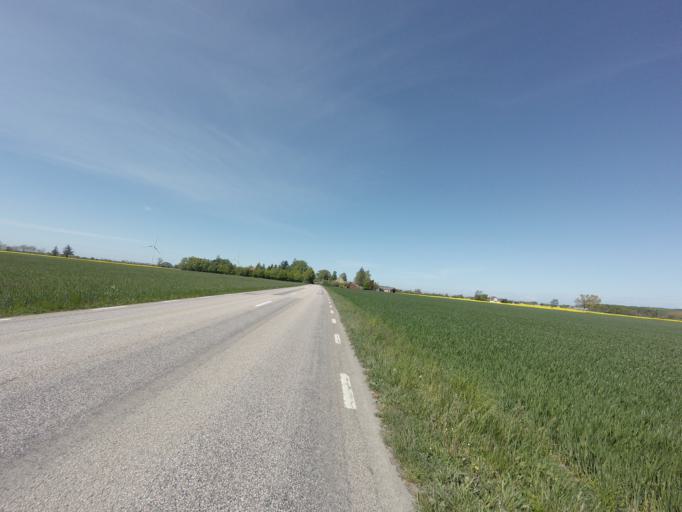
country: SE
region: Skane
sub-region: Helsingborg
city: Odakra
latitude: 56.1411
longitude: 12.6861
